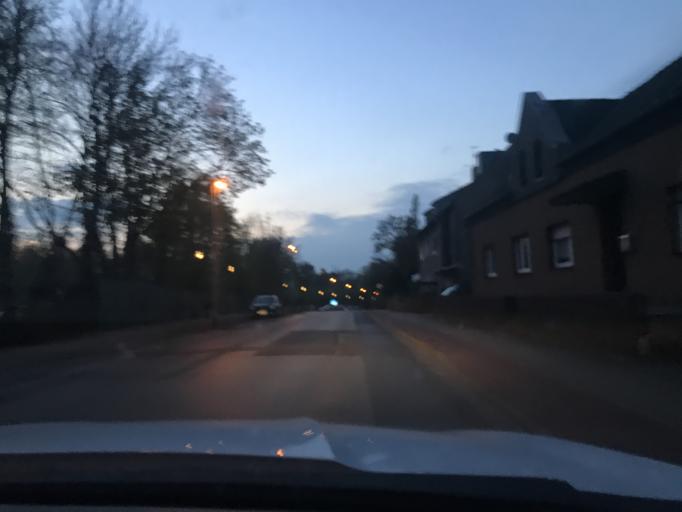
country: DE
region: North Rhine-Westphalia
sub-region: Regierungsbezirk Dusseldorf
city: Hochfeld
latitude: 51.3901
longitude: 6.7048
